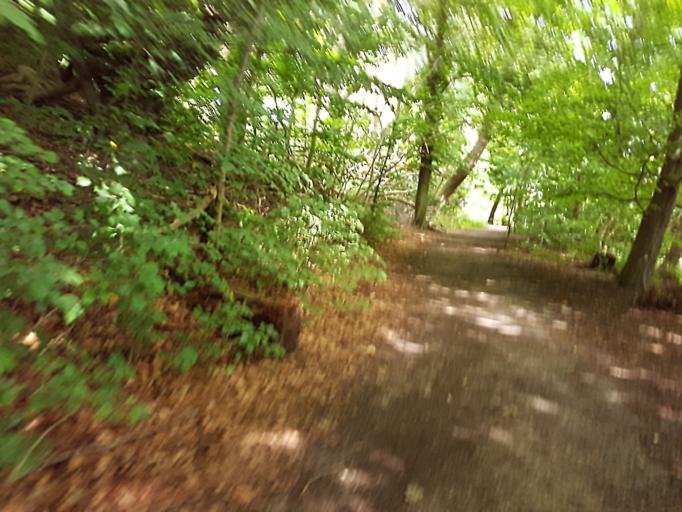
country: DK
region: Capital Region
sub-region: Fureso Kommune
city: Farum
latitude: 55.8035
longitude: 12.3541
